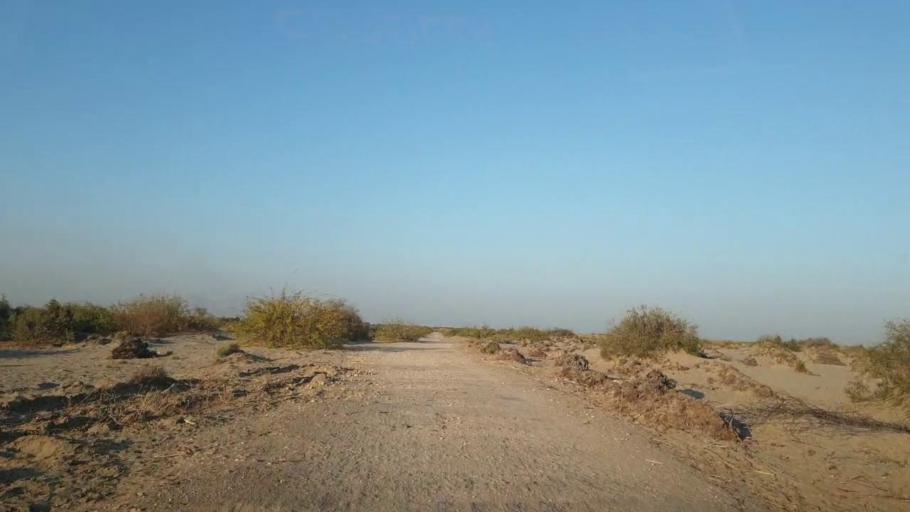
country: PK
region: Sindh
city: Mirpur Khas
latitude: 25.6799
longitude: 69.0483
